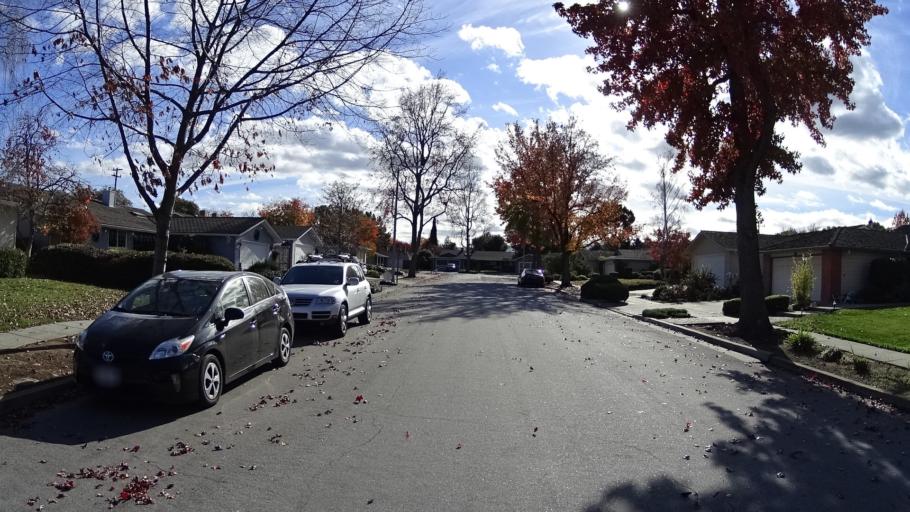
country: US
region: California
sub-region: Santa Clara County
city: Sunnyvale
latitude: 37.3465
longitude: -122.0490
